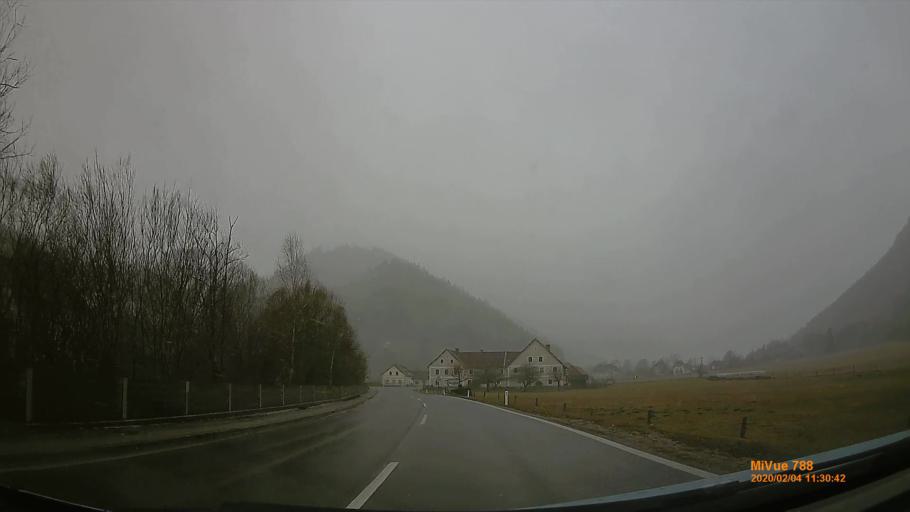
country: AT
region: Styria
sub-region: Politischer Bezirk Bruck-Muerzzuschlag
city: Neuberg an der Muerz
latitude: 47.6566
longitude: 15.5984
